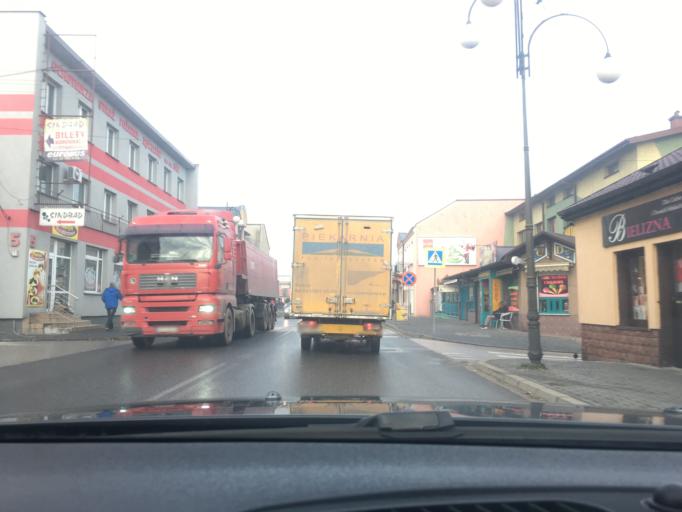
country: PL
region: Swietokrzyskie
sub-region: Powiat jedrzejowski
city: Jedrzejow
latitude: 50.6403
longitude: 20.3036
